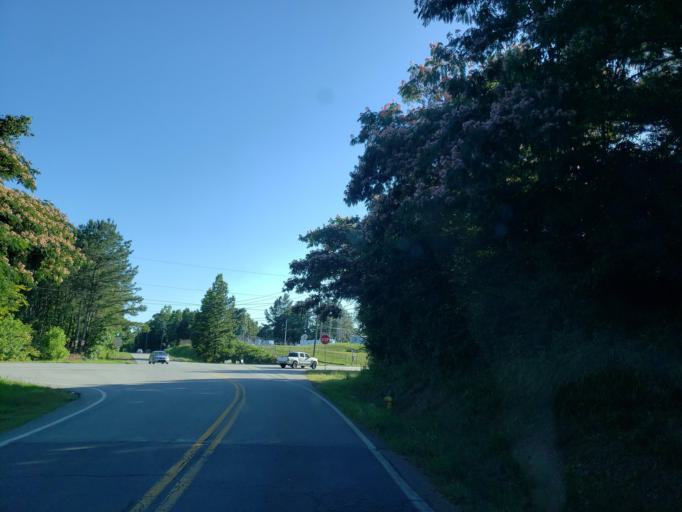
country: US
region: Georgia
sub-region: Floyd County
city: Shannon
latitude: 34.3812
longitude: -85.1303
